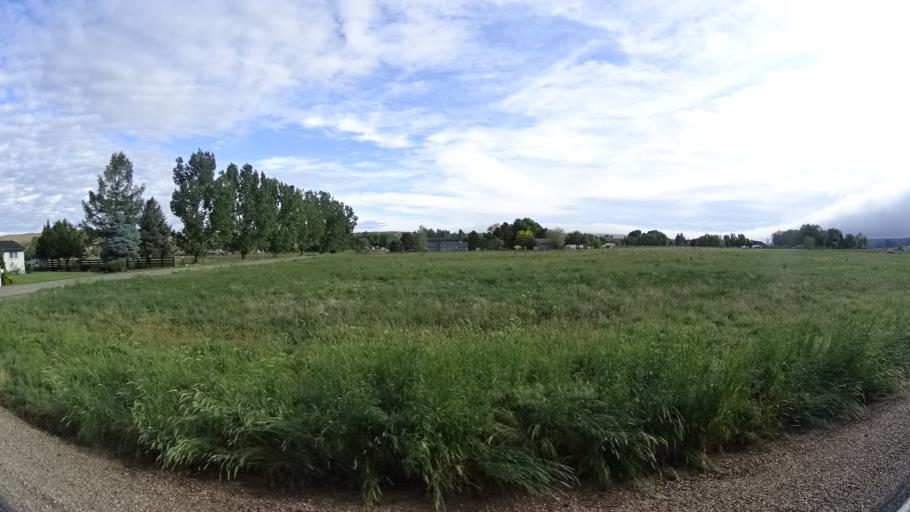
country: US
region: Idaho
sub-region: Ada County
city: Star
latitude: 43.7718
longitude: -116.4852
